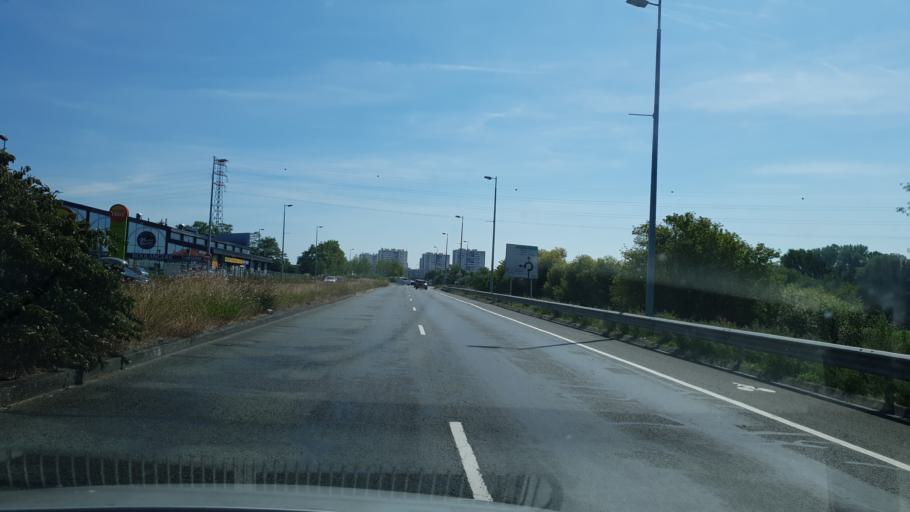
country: FR
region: Centre
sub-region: Departement d'Indre-et-Loire
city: La Riche
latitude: 47.3750
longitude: 0.6689
